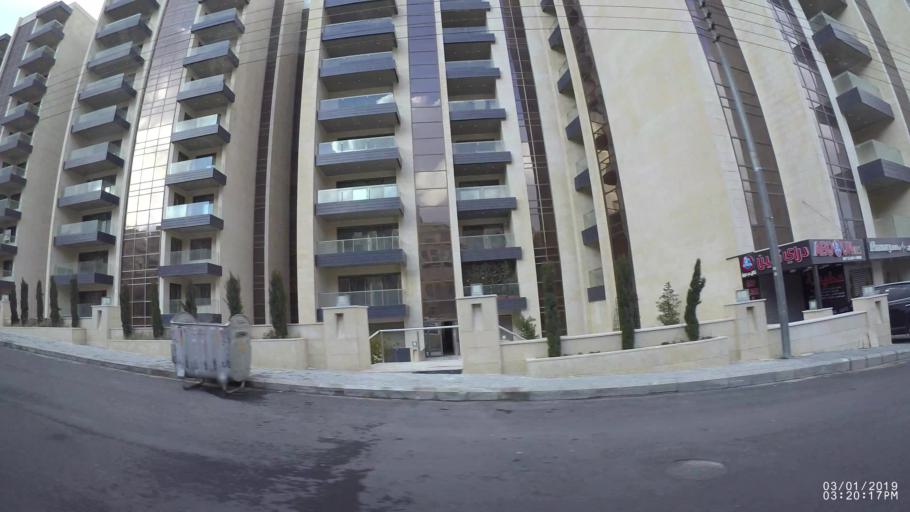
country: JO
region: Amman
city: Al Bunayyat ash Shamaliyah
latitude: 31.9428
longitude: 35.8940
